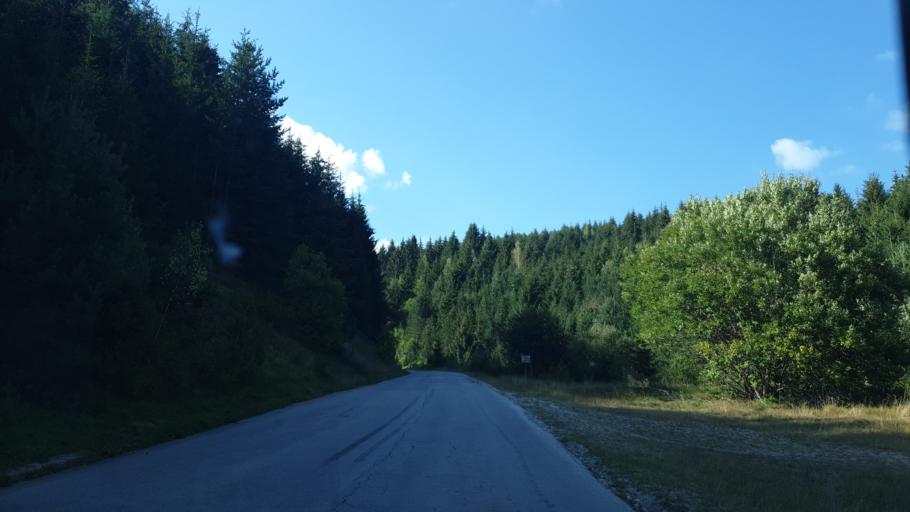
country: RS
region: Central Serbia
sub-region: Zlatiborski Okrug
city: Nova Varos
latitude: 43.4237
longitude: 19.9213
